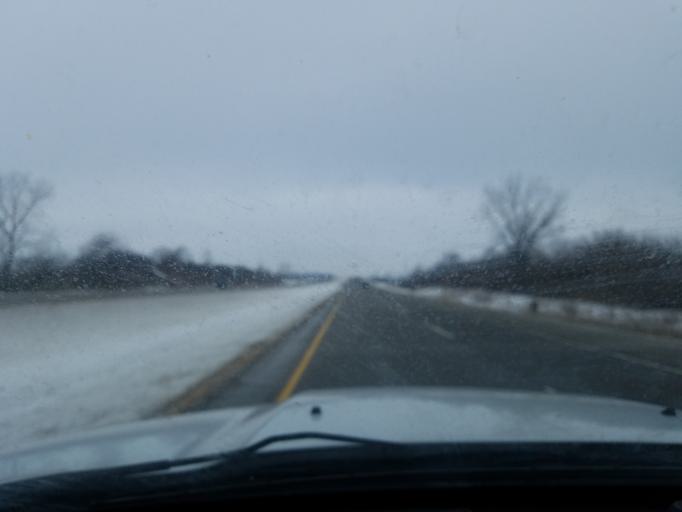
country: US
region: Indiana
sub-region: Marshall County
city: Argos
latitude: 41.2276
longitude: -86.2610
